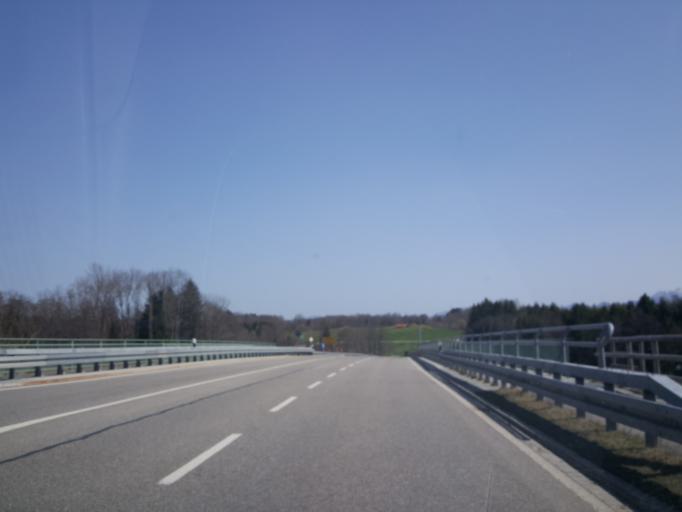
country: DE
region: Bavaria
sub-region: Upper Bavaria
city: Saulgrub
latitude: 47.6703
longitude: 11.0296
